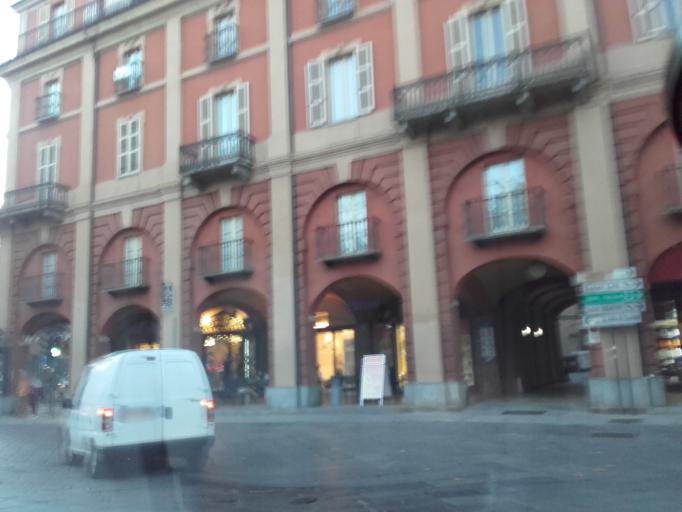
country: IT
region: Piedmont
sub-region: Provincia di Asti
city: Asti
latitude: 44.9008
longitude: 8.2069
